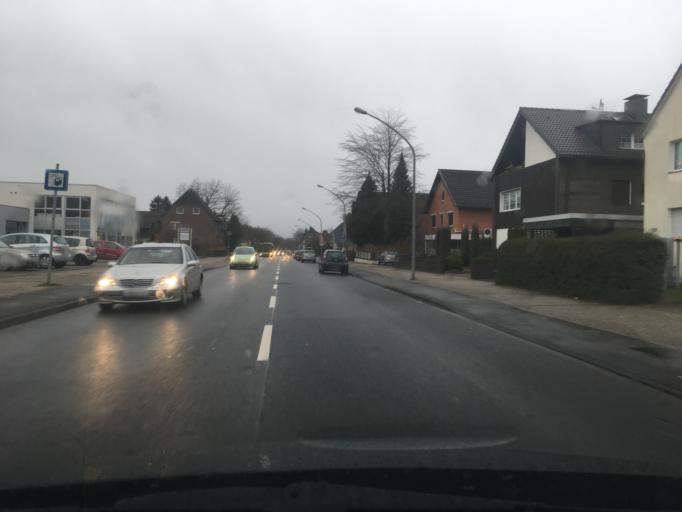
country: DE
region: North Rhine-Westphalia
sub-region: Regierungsbezirk Dusseldorf
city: Oberhausen
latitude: 51.5518
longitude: 6.8435
